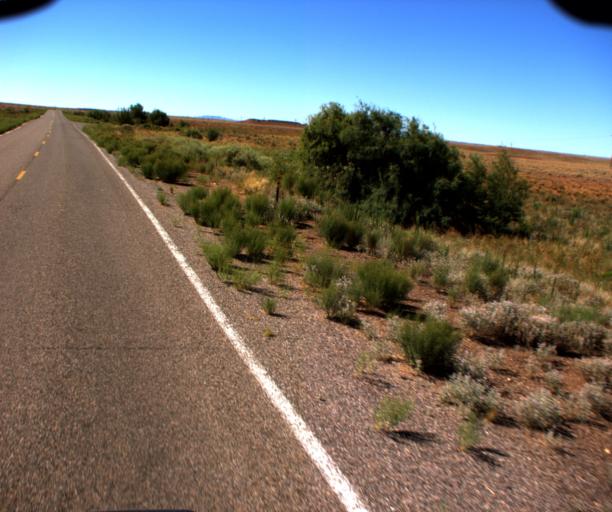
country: US
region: Arizona
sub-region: Coconino County
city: LeChee
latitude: 35.2326
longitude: -110.9576
